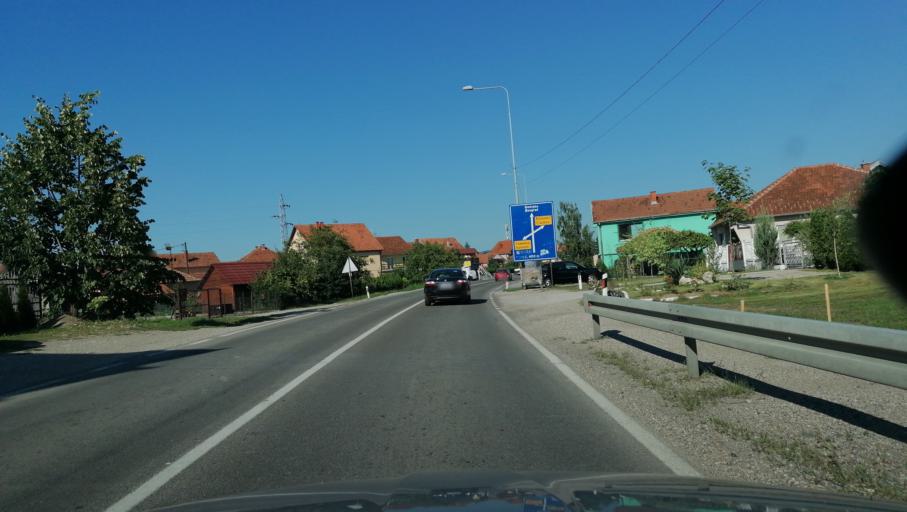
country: RS
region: Central Serbia
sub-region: Raski Okrug
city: Kraljevo
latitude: 43.7295
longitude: 20.6500
